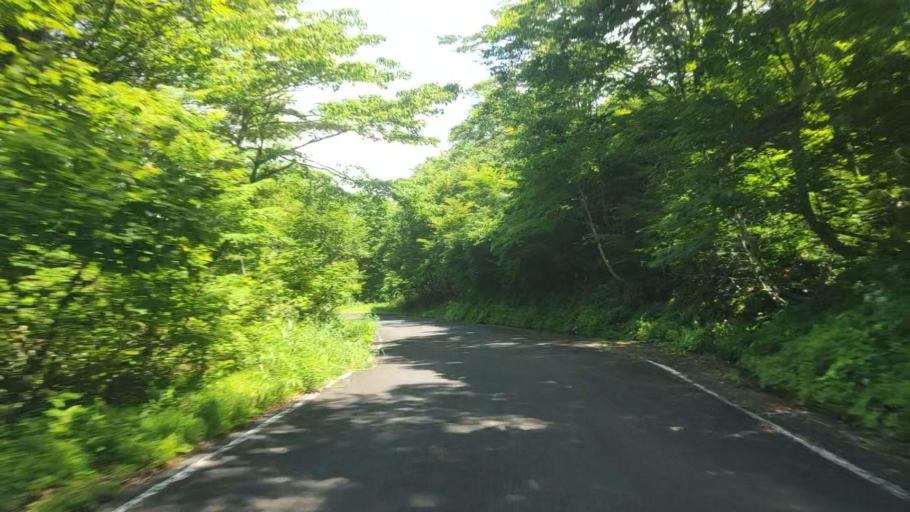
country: JP
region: Fukui
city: Ono
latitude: 35.7749
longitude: 136.5264
